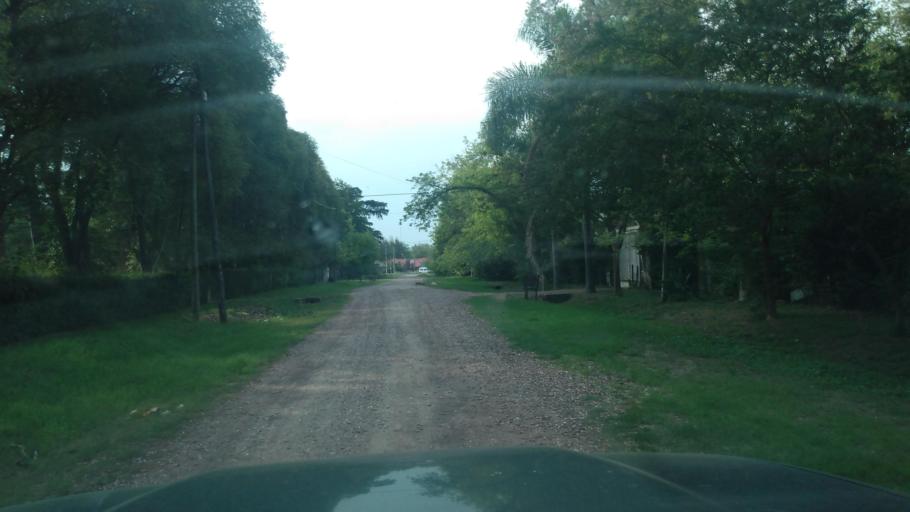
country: AR
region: Buenos Aires
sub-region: Partido de Lujan
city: Lujan
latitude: -34.5515
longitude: -59.1312
